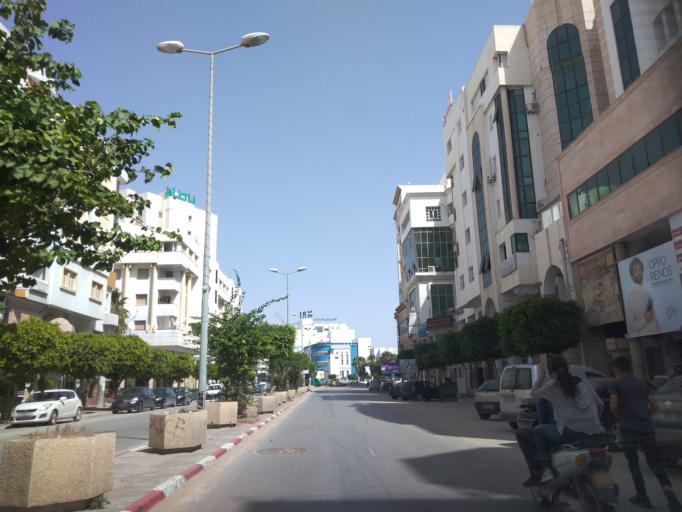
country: TN
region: Safaqis
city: Sfax
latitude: 34.7400
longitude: 10.7534
